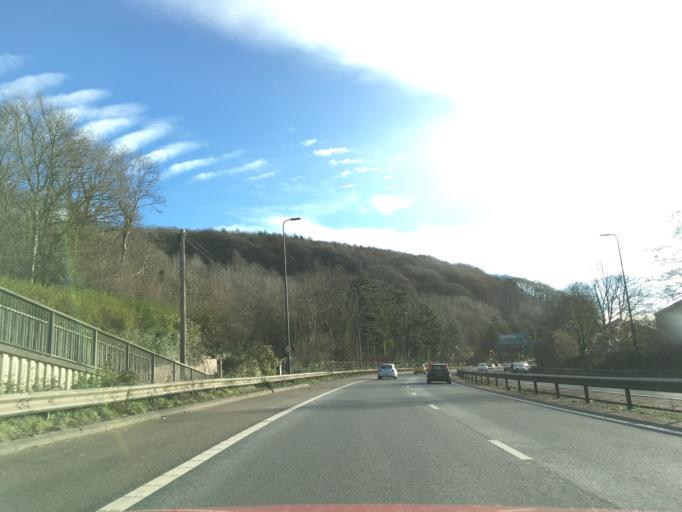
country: GB
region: Wales
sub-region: Cardiff
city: Radyr
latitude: 51.5433
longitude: -3.2623
